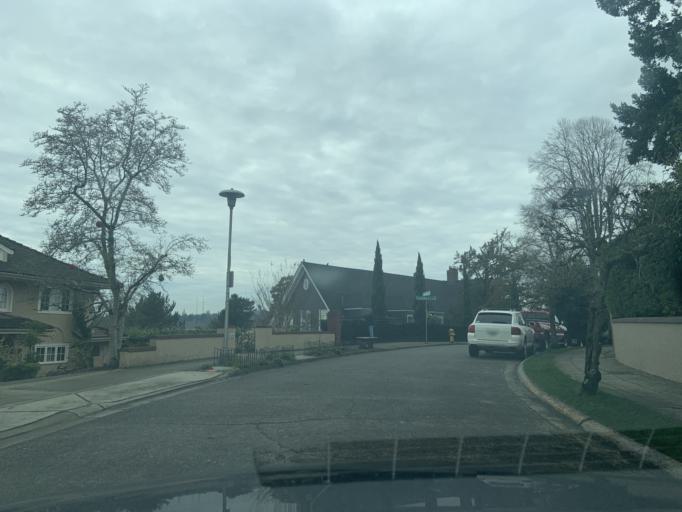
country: US
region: Washington
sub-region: King County
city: Medina
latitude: 47.6492
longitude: -122.2763
